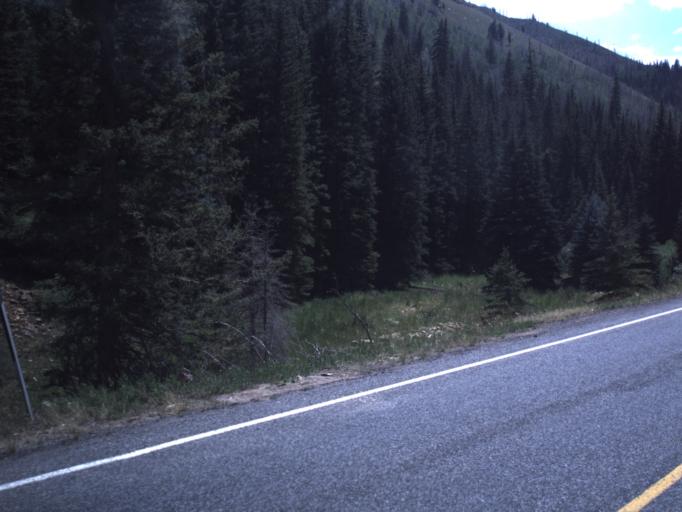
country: US
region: Utah
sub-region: Emery County
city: Huntington
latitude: 39.5101
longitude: -111.1564
